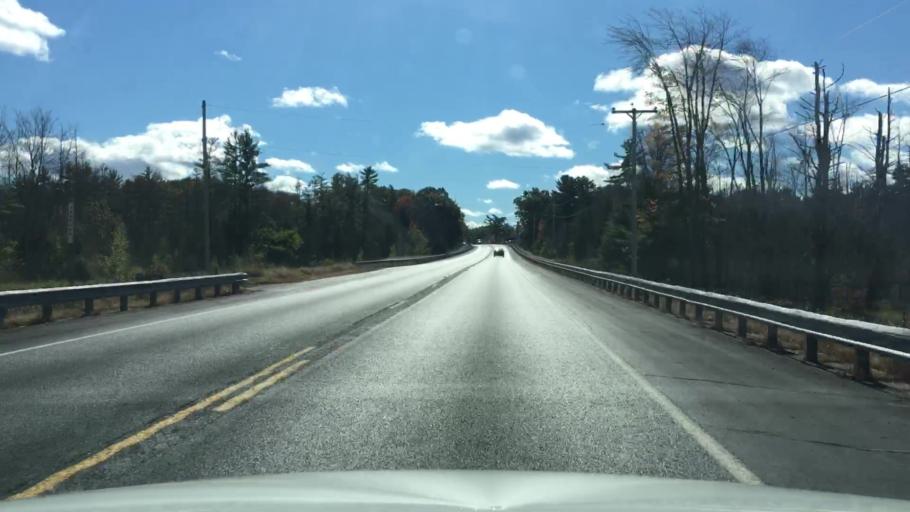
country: US
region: Maine
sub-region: York County
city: South Sanford
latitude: 43.4429
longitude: -70.7311
